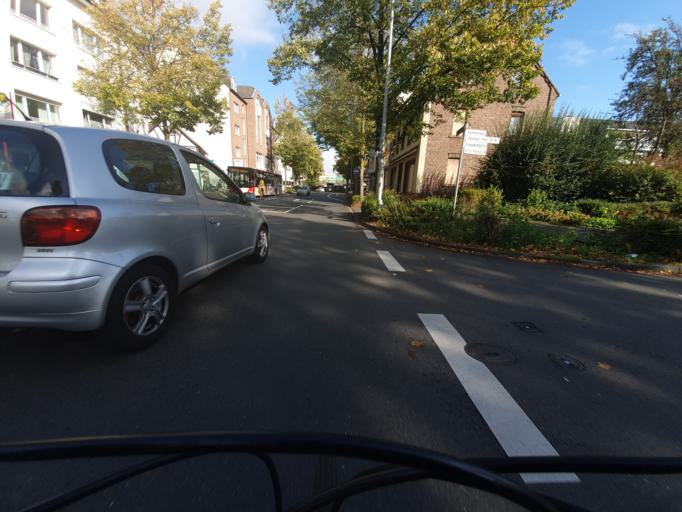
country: DE
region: North Rhine-Westphalia
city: Opladen
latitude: 51.0329
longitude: 7.0476
